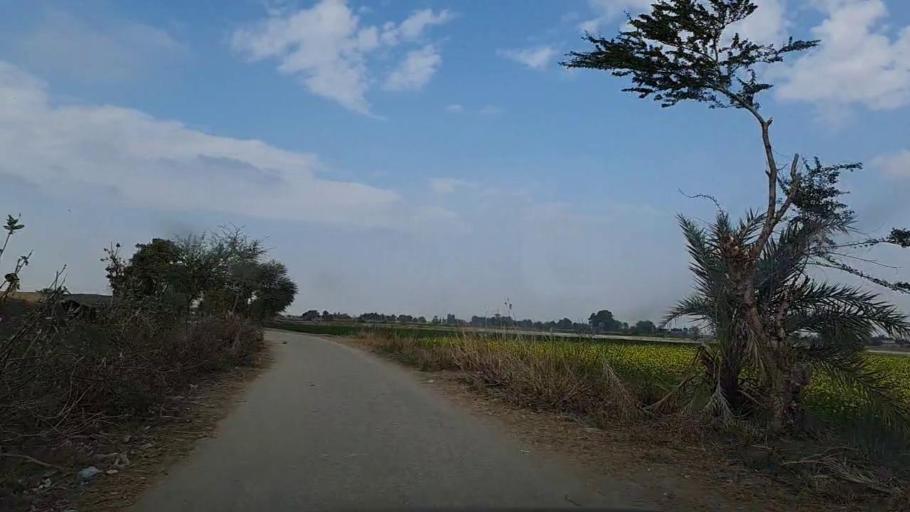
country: PK
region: Sindh
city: Sanghar
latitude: 26.2322
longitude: 69.0200
